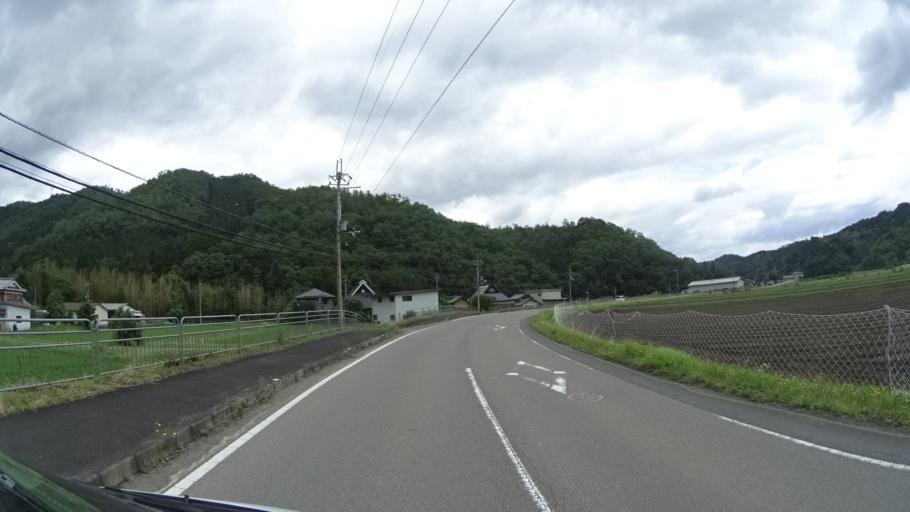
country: JP
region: Kyoto
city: Kameoka
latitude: 35.0949
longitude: 135.4278
